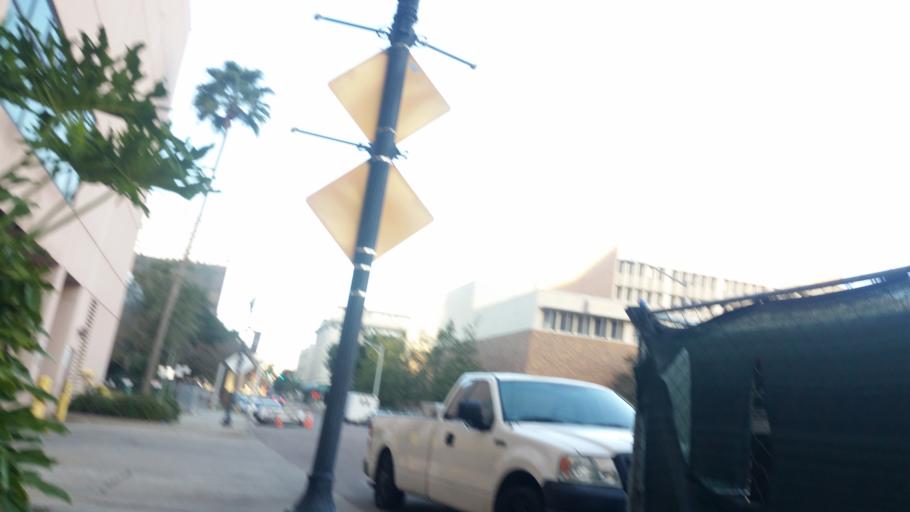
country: US
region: Florida
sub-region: Duval County
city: Jacksonville
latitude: 30.3241
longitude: -81.6548
